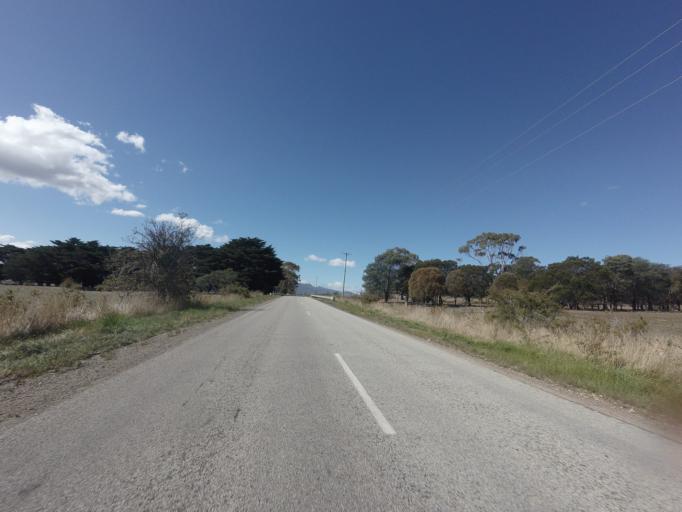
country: AU
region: Tasmania
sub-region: Break O'Day
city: St Helens
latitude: -41.6181
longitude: 148.0061
